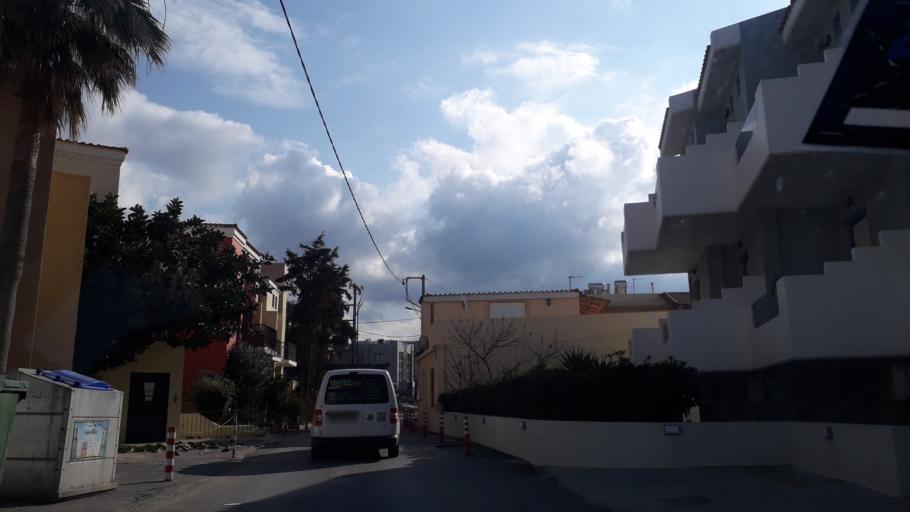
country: GR
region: Crete
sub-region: Nomos Rethymnis
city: Rethymno
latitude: 35.3680
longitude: 24.5044
